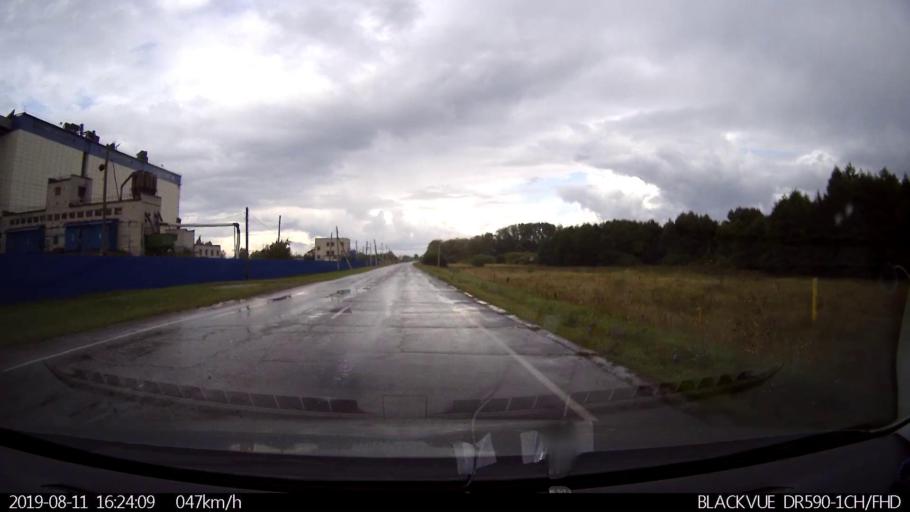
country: RU
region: Ulyanovsk
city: Mayna
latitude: 54.0988
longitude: 47.5918
